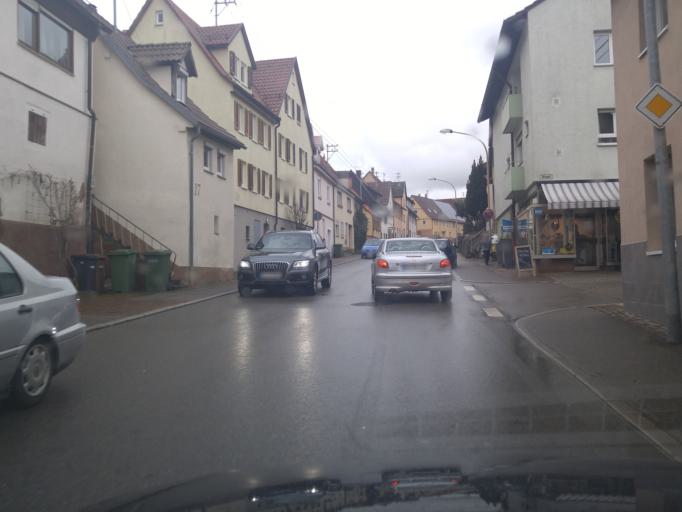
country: DE
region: Baden-Wuerttemberg
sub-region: Regierungsbezirk Stuttgart
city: Erdmannhausen
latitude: 48.9407
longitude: 9.2983
